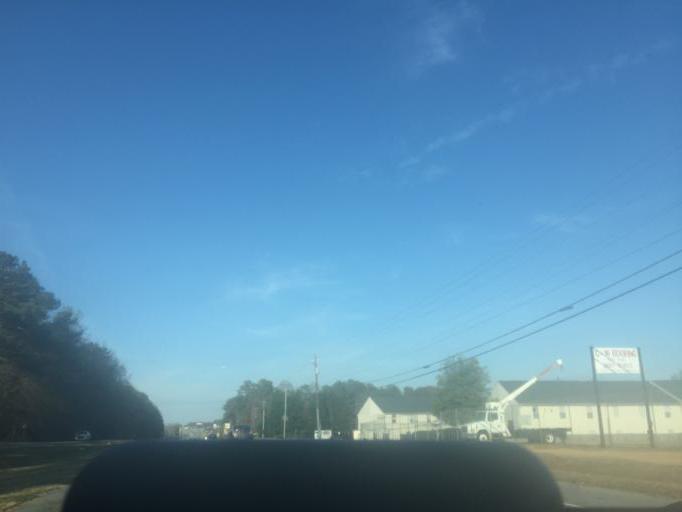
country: US
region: Georgia
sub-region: Clayton County
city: Riverdale
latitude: 33.5959
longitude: -84.4072
